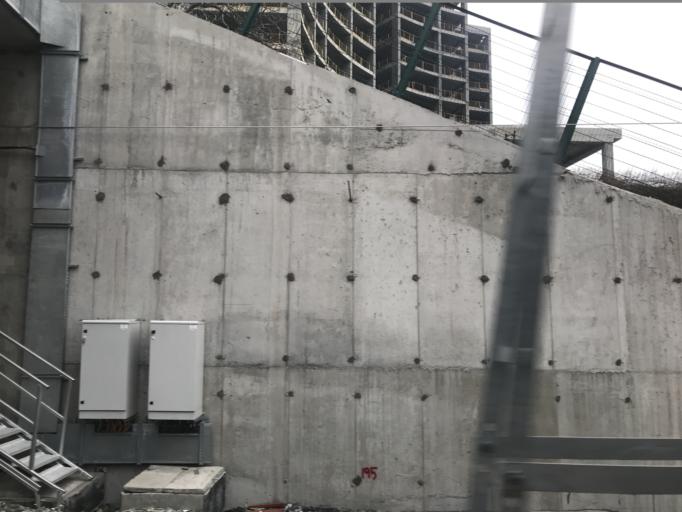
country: TR
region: Istanbul
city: Zeytinburnu
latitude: 40.9865
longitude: 28.9067
